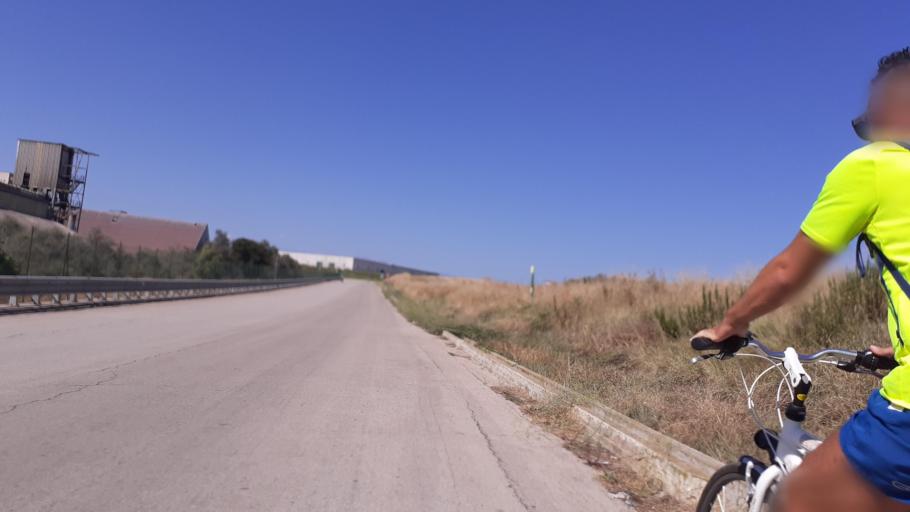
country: IT
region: Abruzzo
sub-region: Provincia di Chieti
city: Vasto
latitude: 42.1709
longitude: 14.7082
